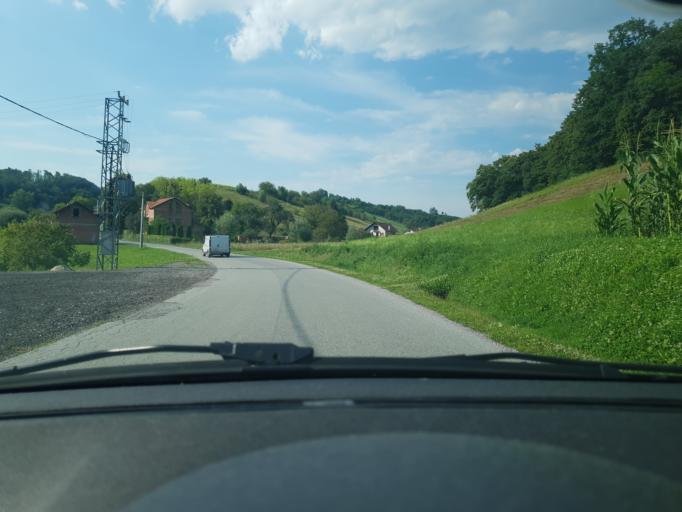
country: HR
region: Zagrebacka
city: Jakovlje
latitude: 46.0102
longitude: 15.8410
